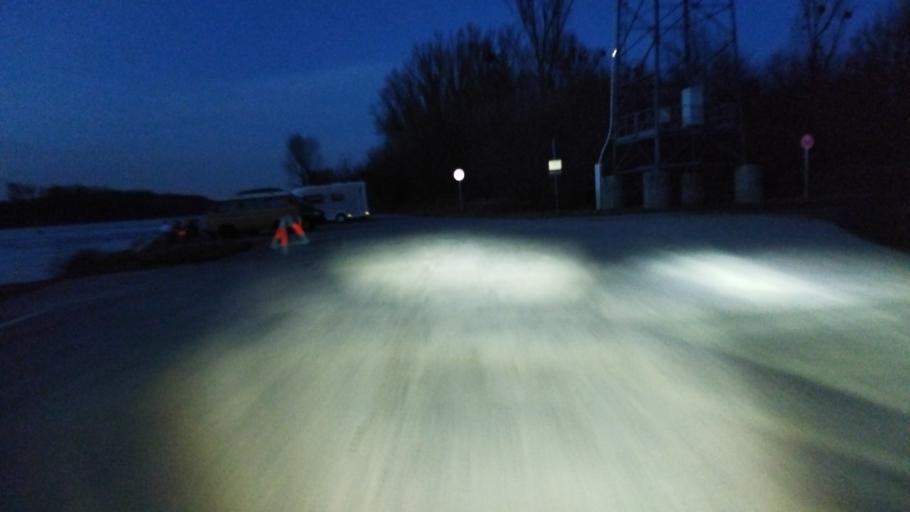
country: DE
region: Rheinland-Pfalz
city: Leimersheim
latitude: 49.1206
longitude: 8.3669
